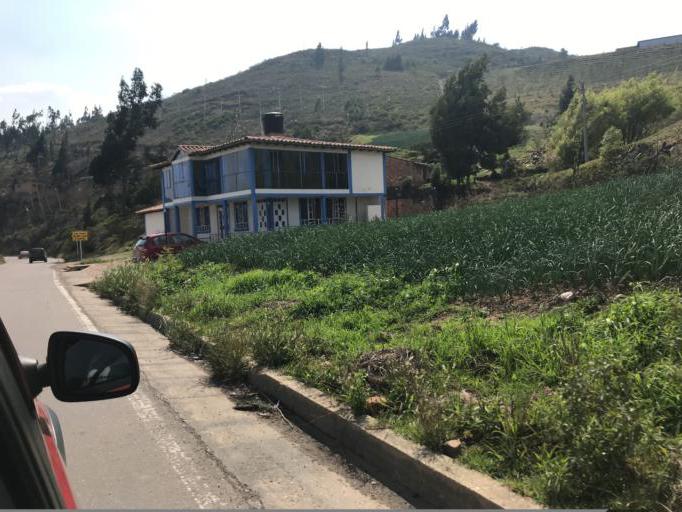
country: CO
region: Boyaca
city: Cucaita
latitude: 5.5458
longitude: -73.4921
